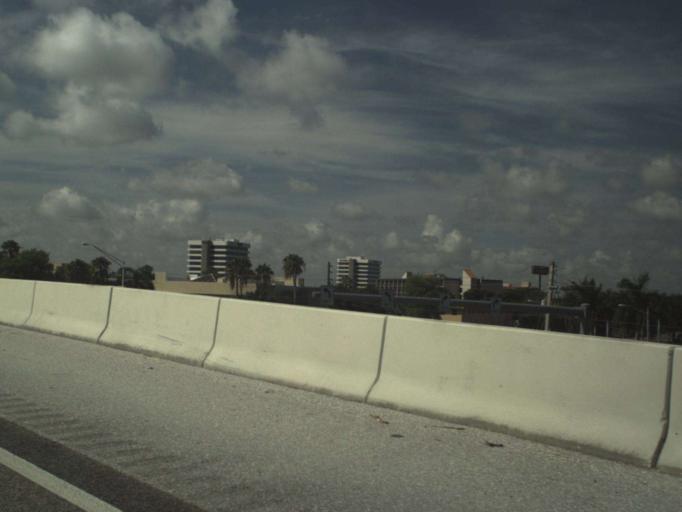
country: US
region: Florida
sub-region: Palm Beach County
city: Schall Circle
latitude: 26.7206
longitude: -80.0908
